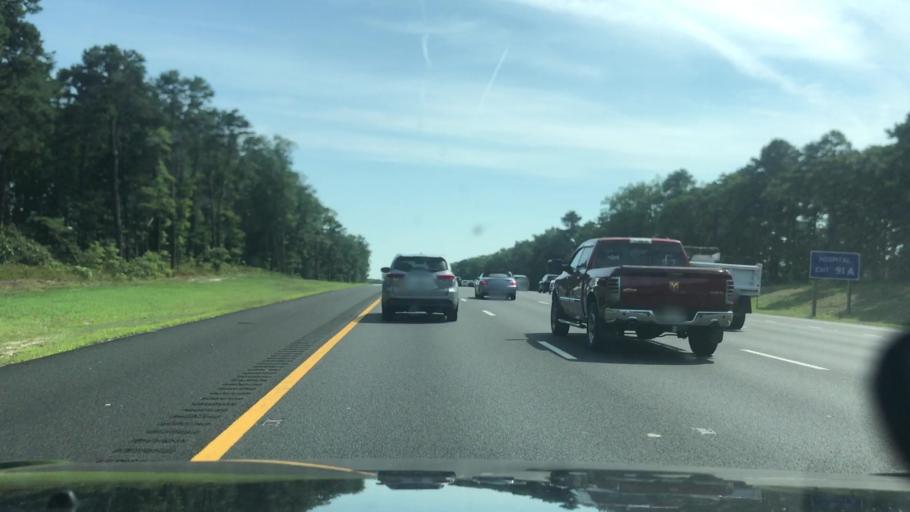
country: US
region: New Jersey
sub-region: Monmouth County
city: Ramtown
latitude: 40.1156
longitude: -74.1311
